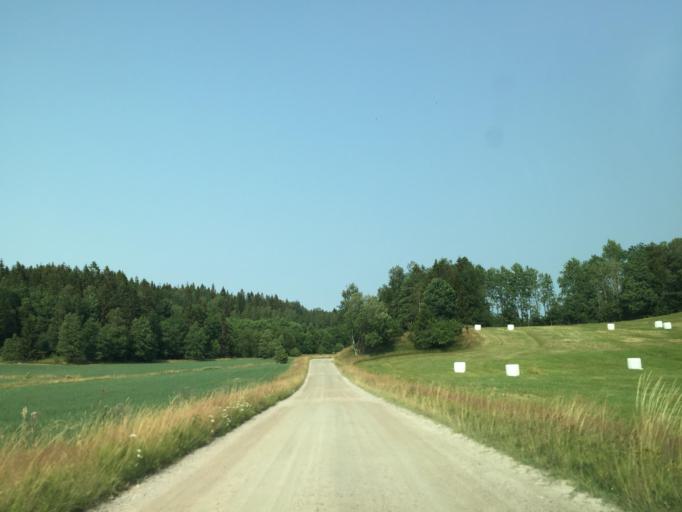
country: SE
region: Vaestra Goetaland
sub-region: Trollhattan
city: Sjuntorp
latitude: 58.2698
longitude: 12.1025
